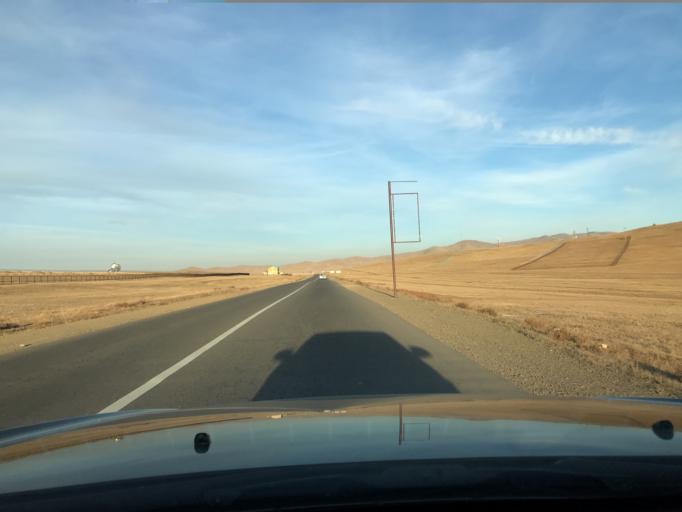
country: MN
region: Central Aimak
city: Arhust
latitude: 47.8009
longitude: 107.5198
